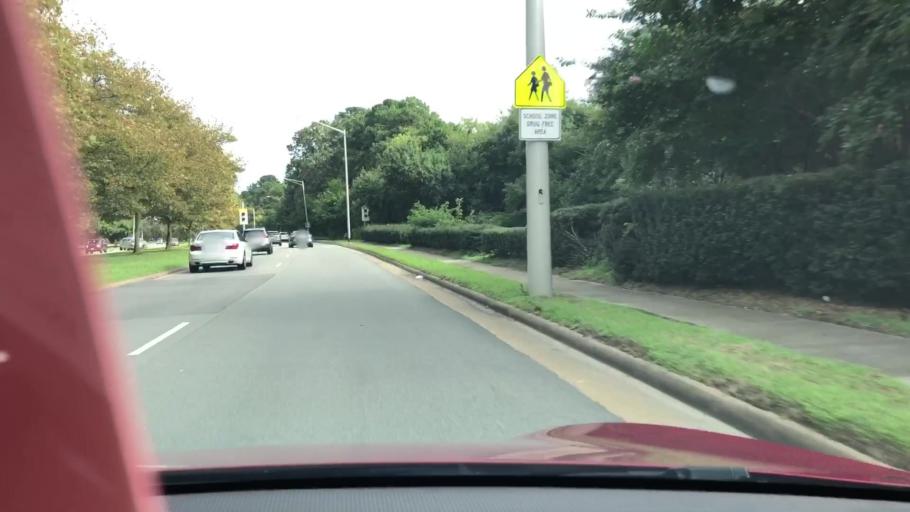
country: US
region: Virginia
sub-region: City of Virginia Beach
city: Virginia Beach
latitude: 36.8991
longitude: -76.0652
